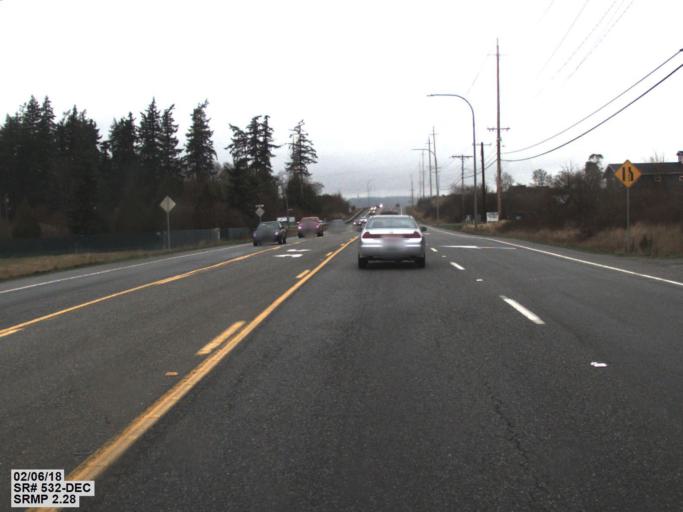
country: US
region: Washington
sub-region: Snohomish County
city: Stanwood
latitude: 48.2398
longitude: -122.4084
